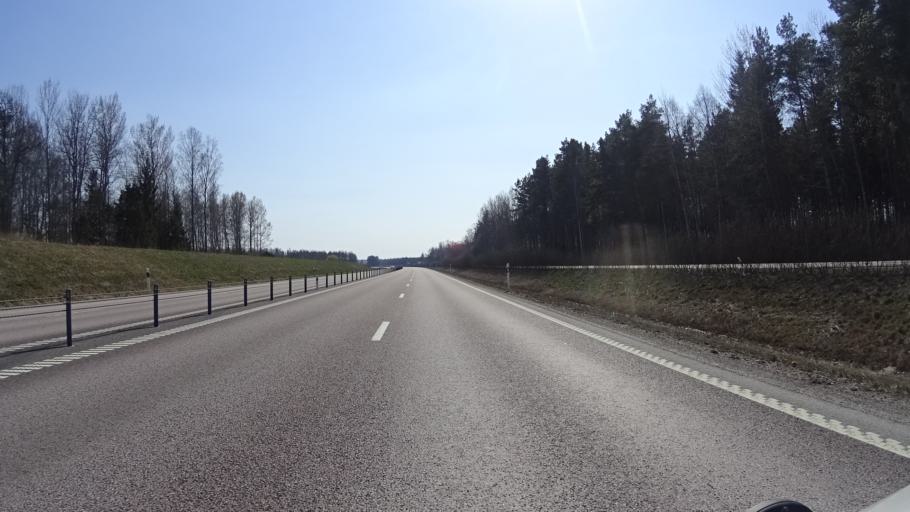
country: SE
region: OEstergoetland
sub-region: Mjolby Kommun
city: Mjolby
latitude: 58.3839
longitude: 15.1044
